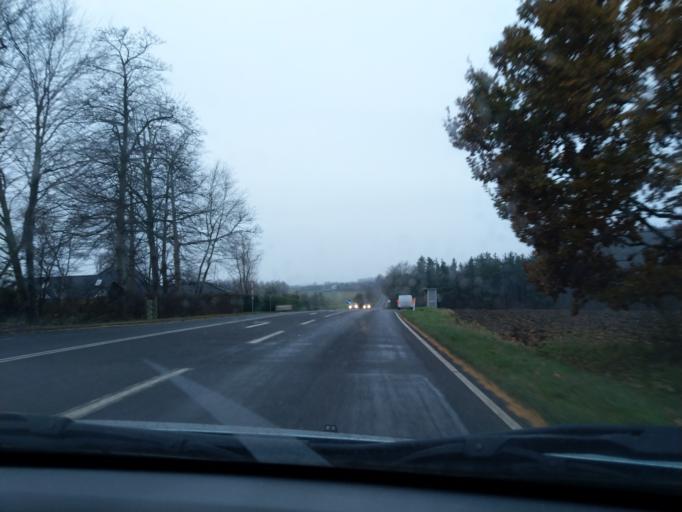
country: DK
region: Zealand
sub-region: Vordingborg Kommune
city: Praesto
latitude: 55.1170
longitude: 11.9954
